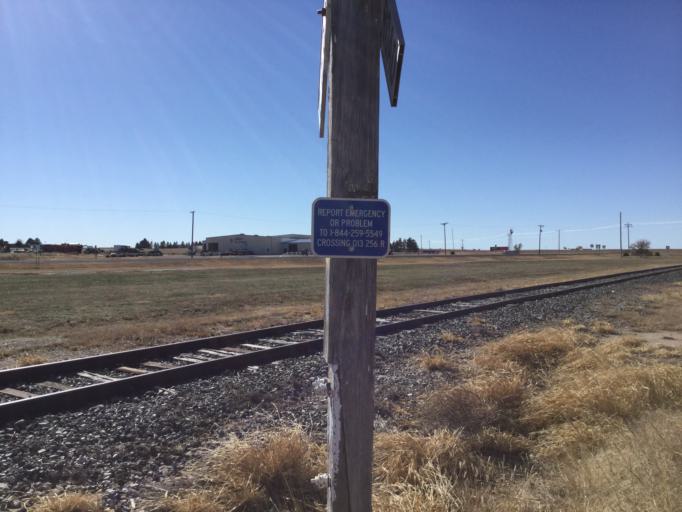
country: US
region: Kansas
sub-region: Morton County
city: Elkhart
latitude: 36.9936
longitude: -101.9008
